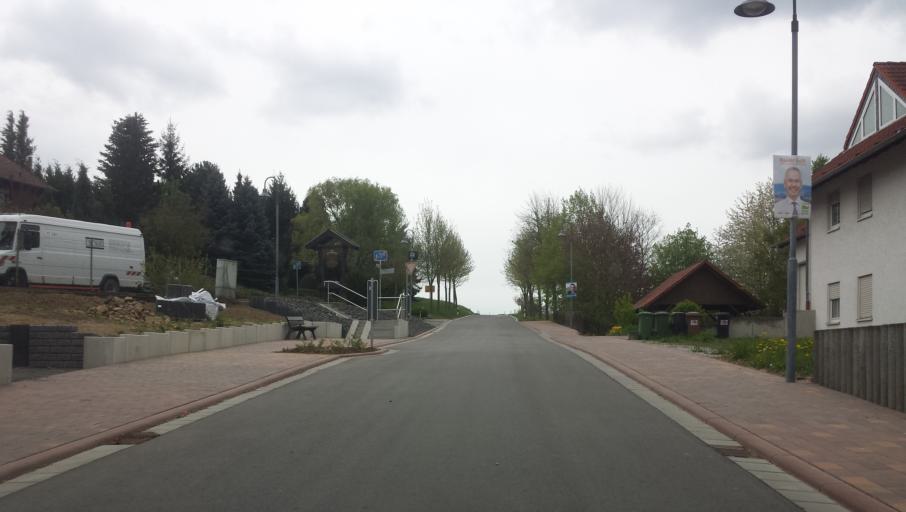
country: DE
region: Rheinland-Pfalz
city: Morsfeld
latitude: 49.7429
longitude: 7.9299
